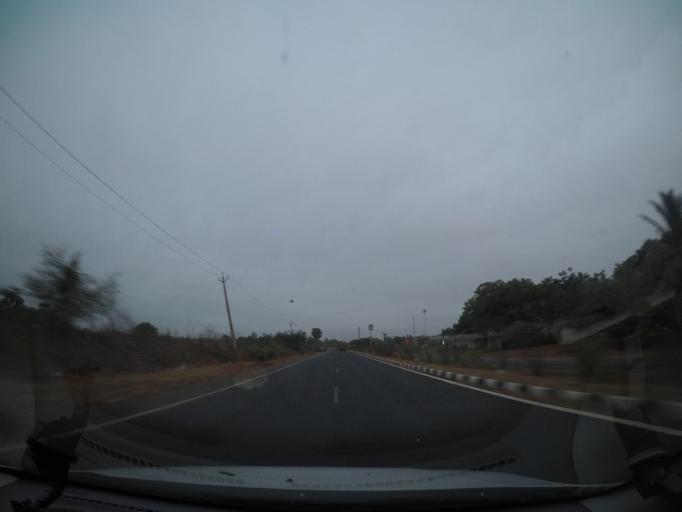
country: IN
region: Andhra Pradesh
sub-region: West Godavari
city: Akividu
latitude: 16.8059
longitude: 81.3079
